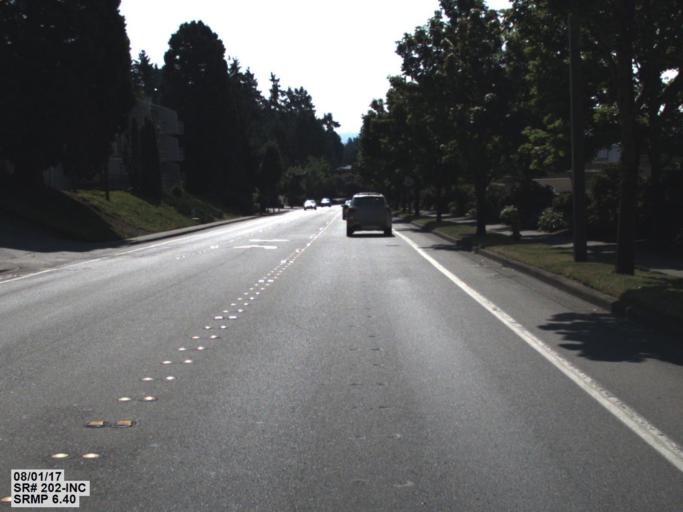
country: US
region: Washington
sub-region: King County
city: Redmond
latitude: 47.6819
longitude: -122.1229
